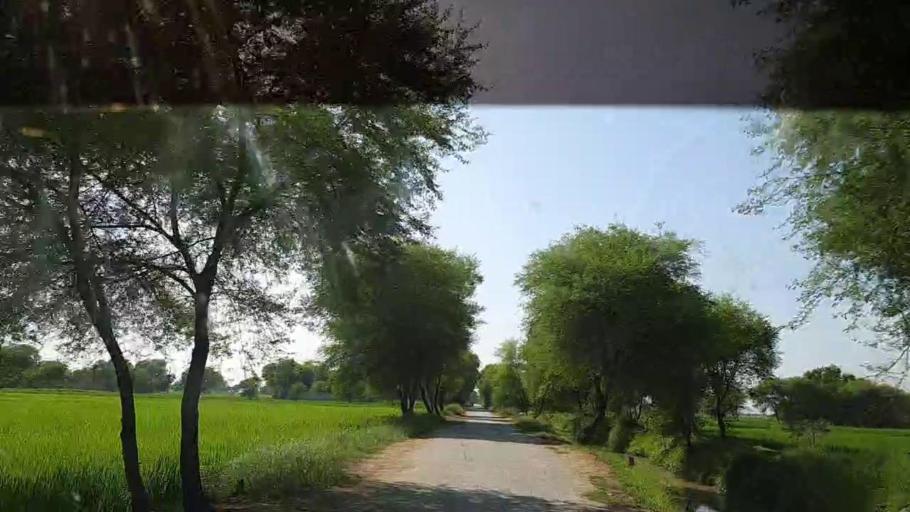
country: PK
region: Sindh
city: Ghauspur
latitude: 28.1741
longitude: 69.0520
